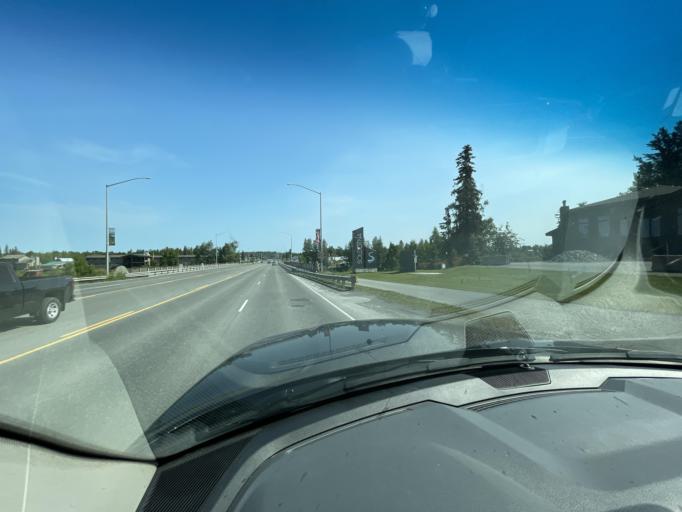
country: US
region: Alaska
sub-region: Kenai Peninsula Borough
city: Soldotna
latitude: 60.4759
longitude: -151.0829
